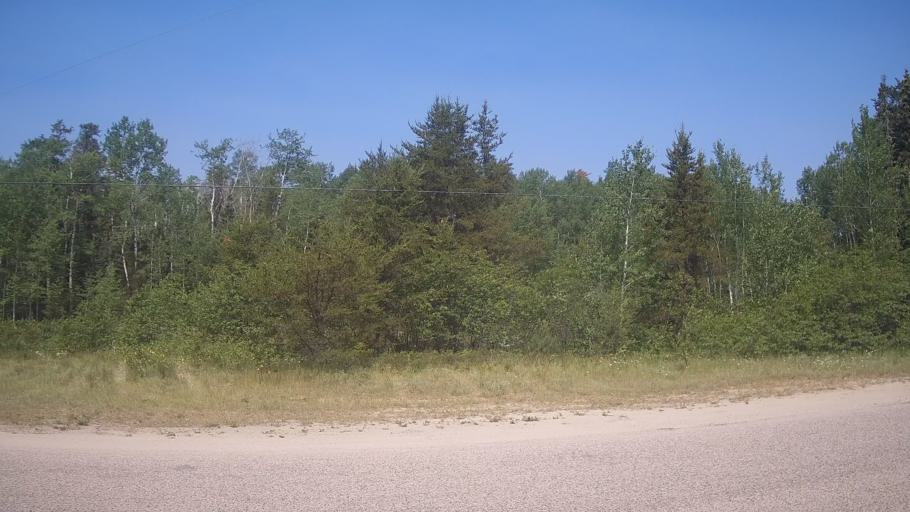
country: CA
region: Ontario
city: Timmins
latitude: 47.6806
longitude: -81.7149
